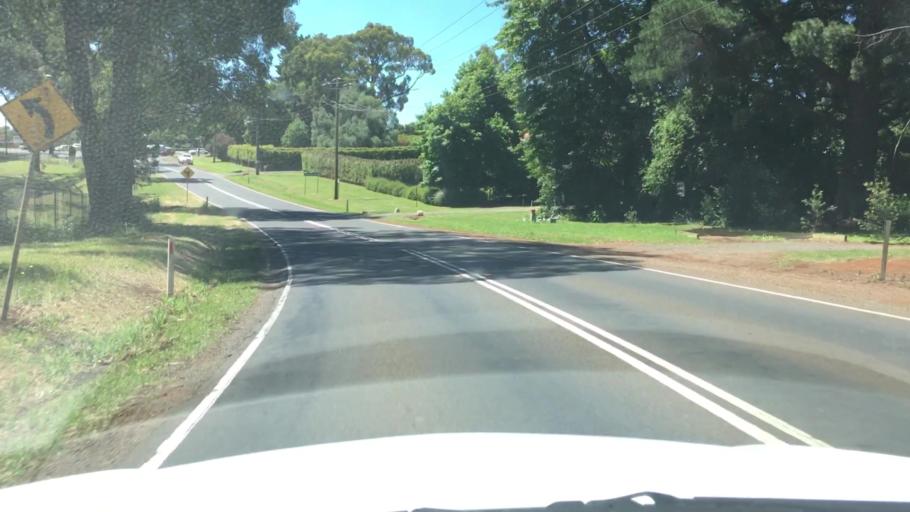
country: AU
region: Victoria
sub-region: Yarra Ranges
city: Monbulk
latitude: -37.8341
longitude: 145.4296
